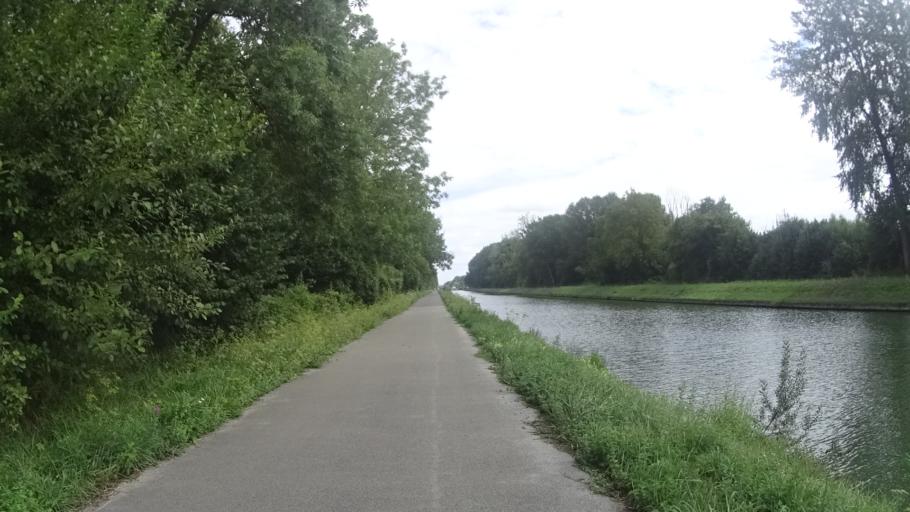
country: FR
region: Picardie
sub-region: Departement de l'Aisne
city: Blerancourt
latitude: 49.5772
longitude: 3.0985
